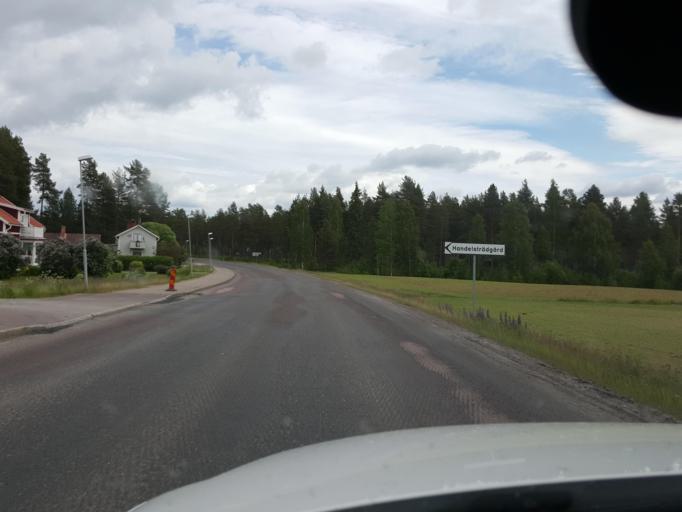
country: SE
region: Gaevleborg
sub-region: Ljusdals Kommun
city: Farila
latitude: 61.8005
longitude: 15.8869
